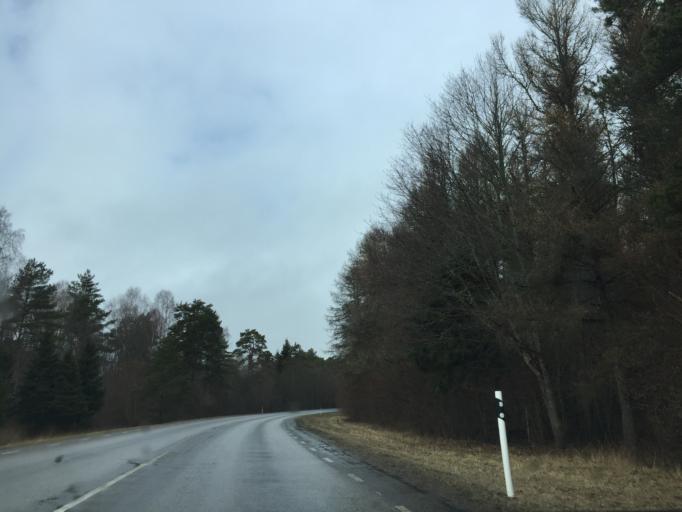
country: EE
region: Laeaene
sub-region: Haapsalu linn
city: Haapsalu
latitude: 58.9160
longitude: 23.5508
